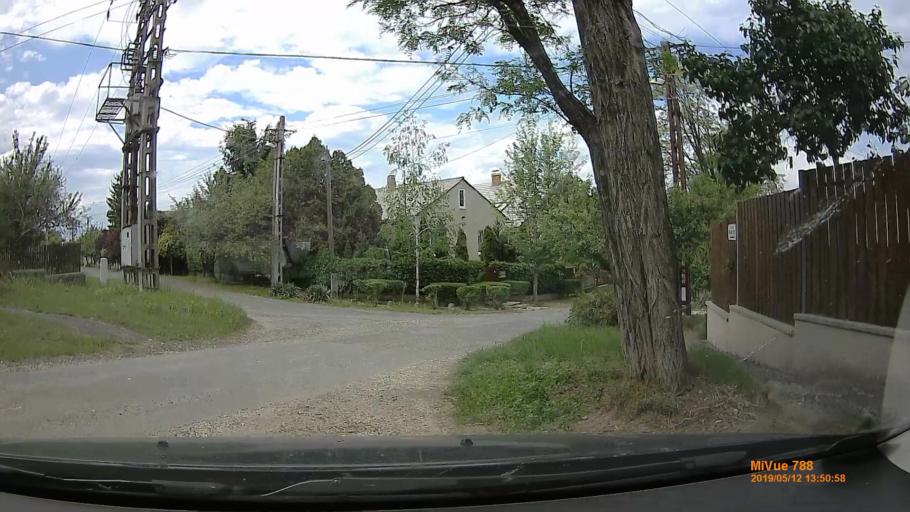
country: HU
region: Pest
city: Pecel
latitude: 47.4890
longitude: 19.3033
